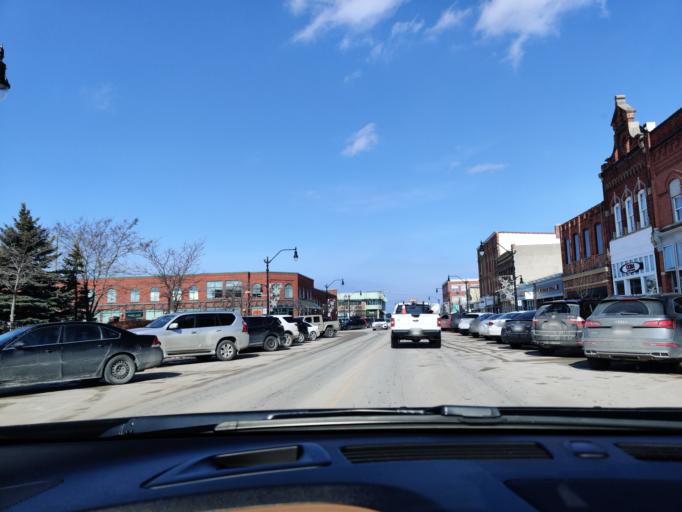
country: CA
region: Ontario
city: Collingwood
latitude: 44.5015
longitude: -80.2171
